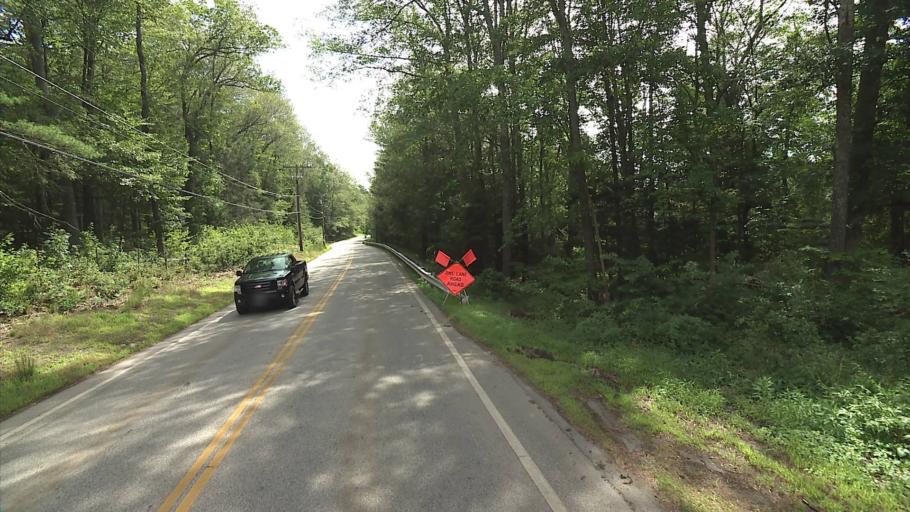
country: US
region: Connecticut
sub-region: Windham County
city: South Woodstock
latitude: 41.9376
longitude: -71.9704
